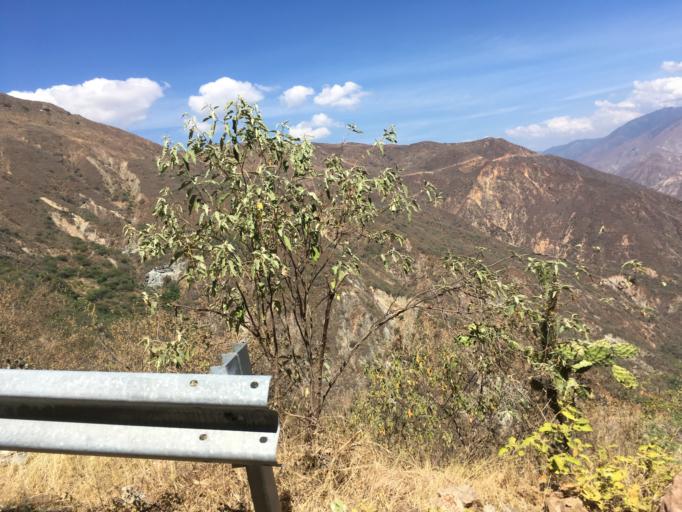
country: CO
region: Santander
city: Aratoca
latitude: 6.7710
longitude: -72.9888
